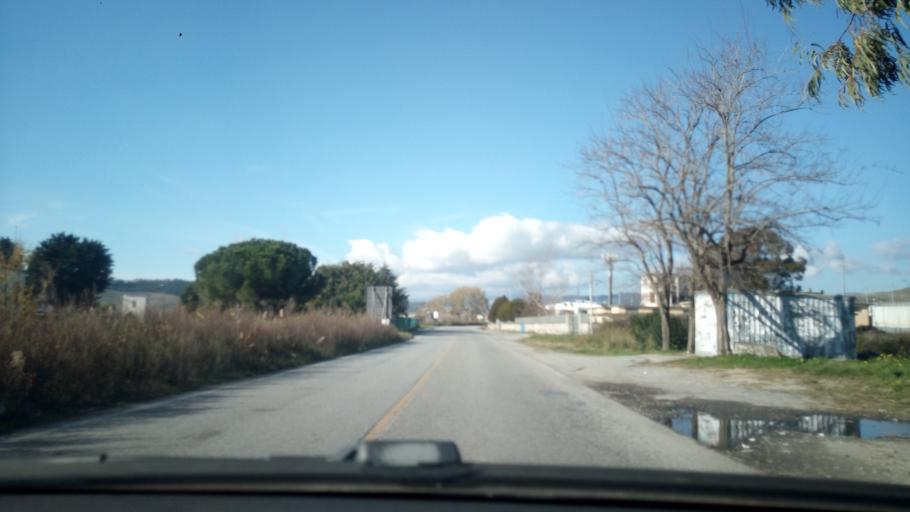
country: IT
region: Calabria
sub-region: Provincia di Catanzaro
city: Catanzaro
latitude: 38.8591
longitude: 16.5698
